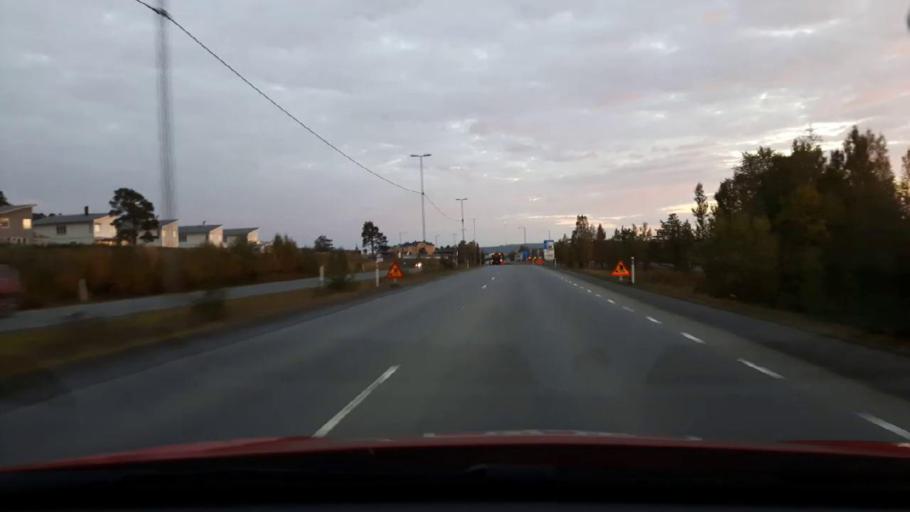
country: SE
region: Jaemtland
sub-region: OEstersunds Kommun
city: Ostersund
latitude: 63.1920
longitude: 14.6424
